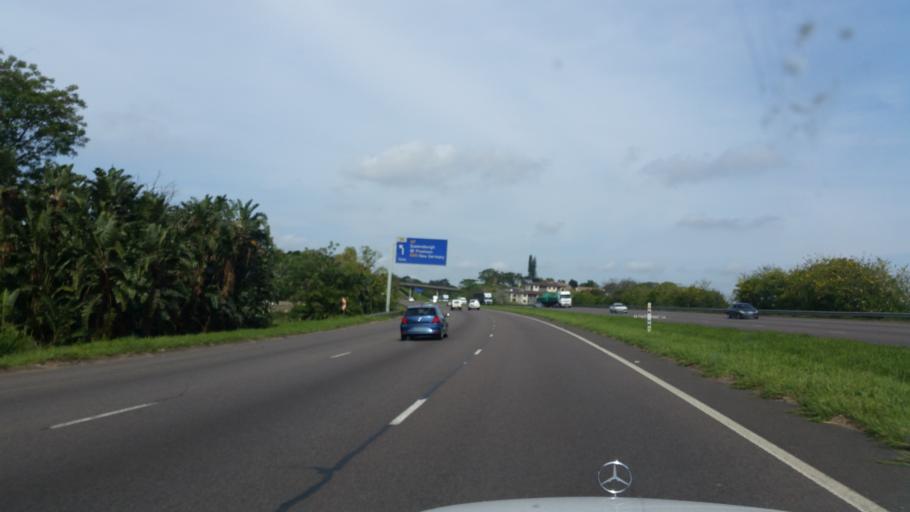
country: ZA
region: KwaZulu-Natal
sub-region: eThekwini Metropolitan Municipality
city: Berea
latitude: -29.8320
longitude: 30.8468
